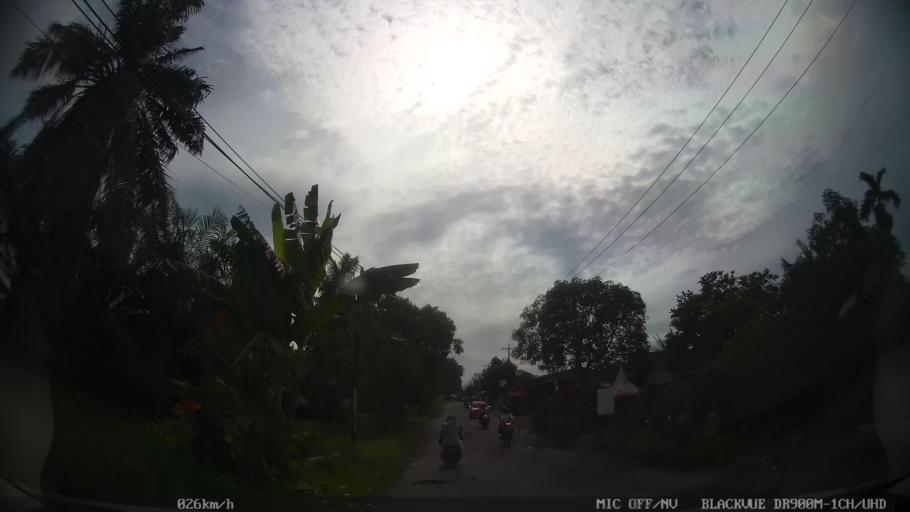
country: ID
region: North Sumatra
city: Medan
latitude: 3.6217
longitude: 98.7110
